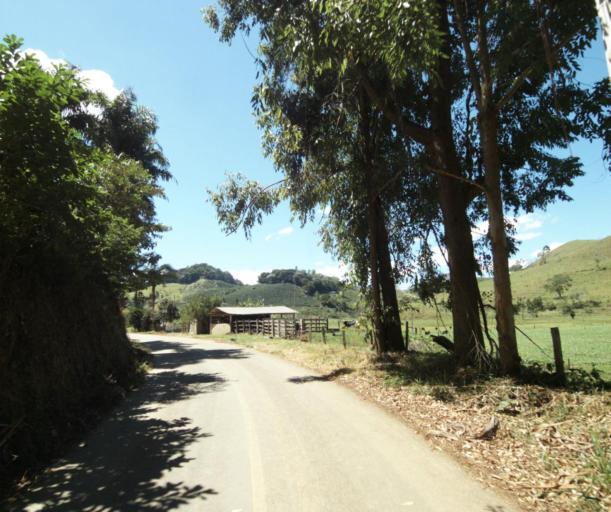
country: BR
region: Minas Gerais
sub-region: Espera Feliz
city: Espera Feliz
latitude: -20.6395
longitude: -41.8156
